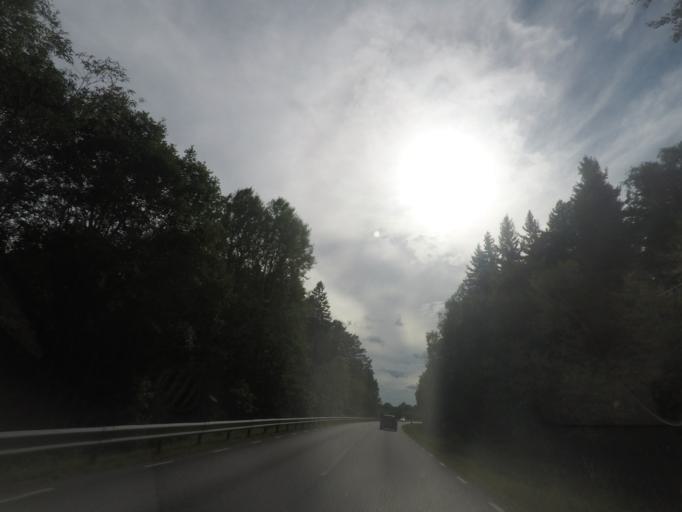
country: SE
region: Stockholm
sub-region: Norrtalje Kommun
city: Skanninge
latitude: 59.9036
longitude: 18.5764
